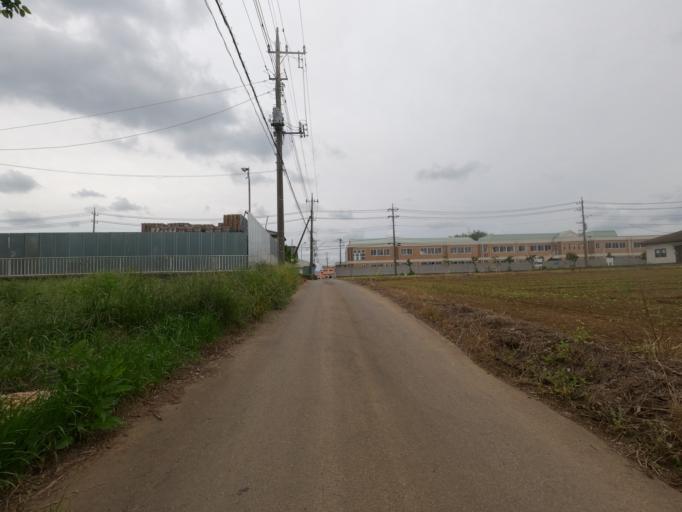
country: JP
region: Ibaraki
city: Moriya
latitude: 35.9521
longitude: 139.9707
